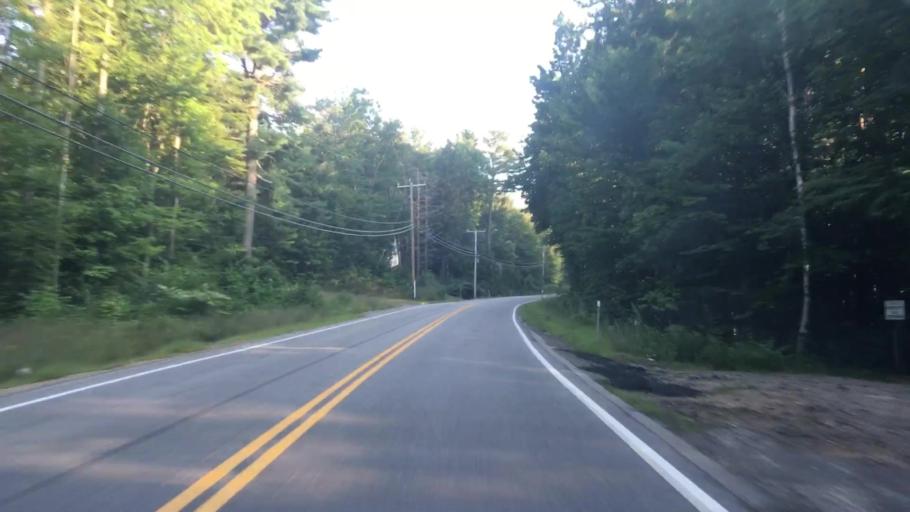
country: US
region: New Hampshire
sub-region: Belknap County
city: Laconia
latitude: 43.5005
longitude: -71.4471
